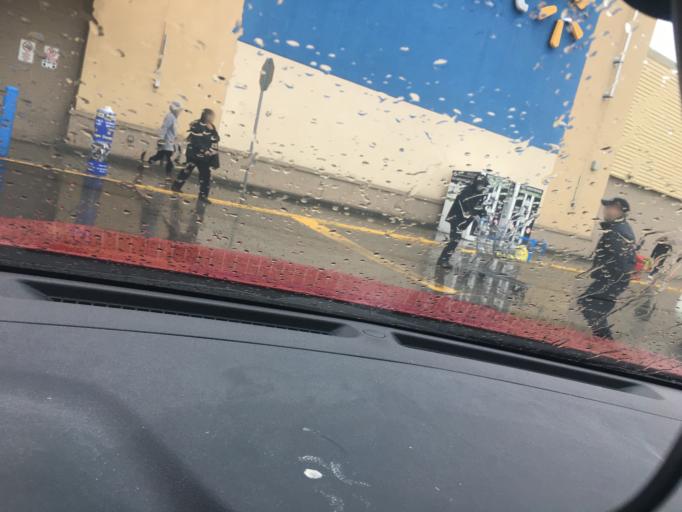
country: CA
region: Ontario
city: Scarborough
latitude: 43.7841
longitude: -79.2909
